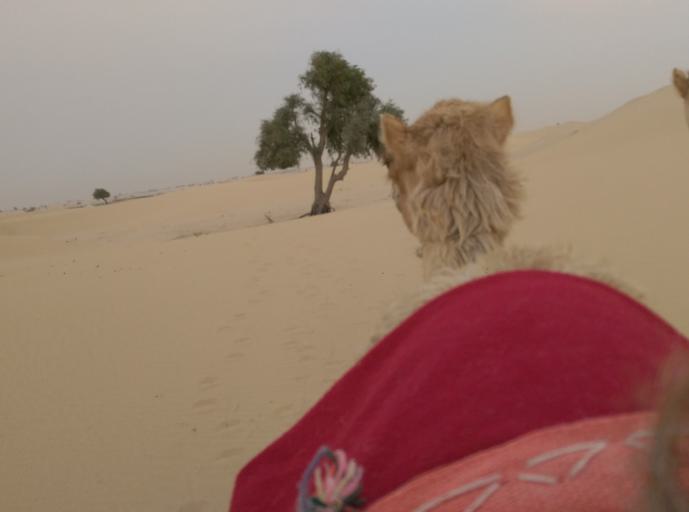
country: AE
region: Dubai
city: Dubai
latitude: 24.9345
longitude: 55.3726
